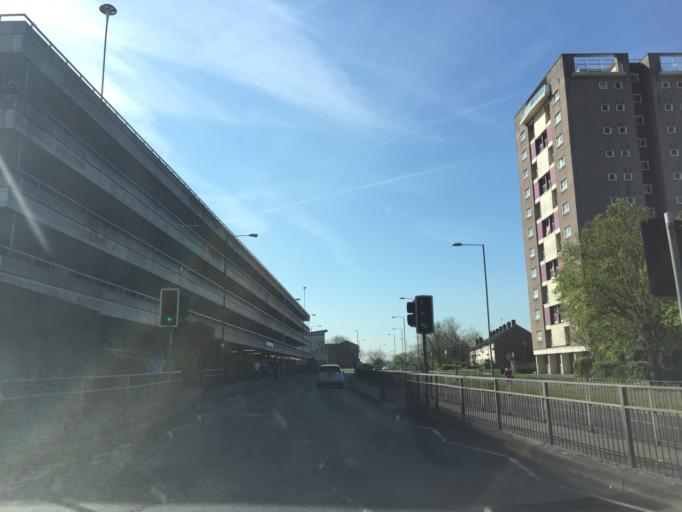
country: GB
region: England
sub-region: Essex
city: Harlow
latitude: 51.7696
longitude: 0.0900
